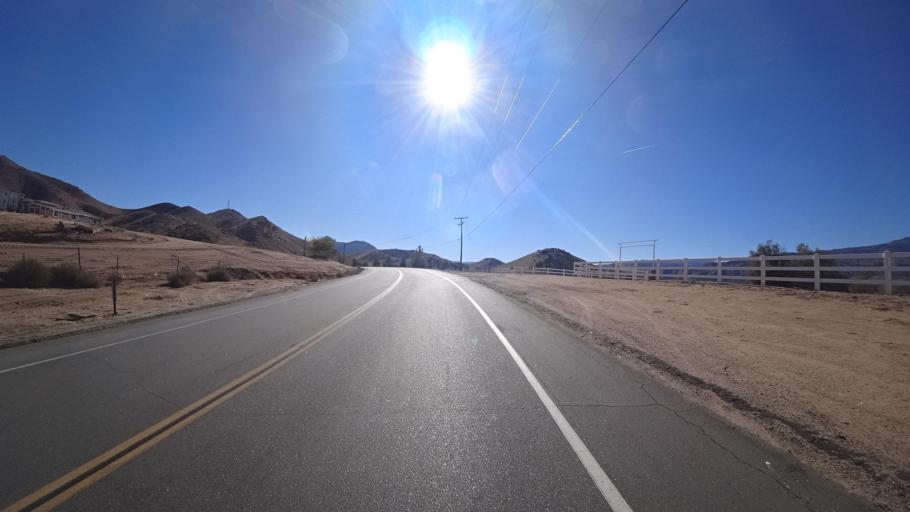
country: US
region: California
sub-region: Kern County
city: Wofford Heights
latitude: 35.7070
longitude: -118.4229
